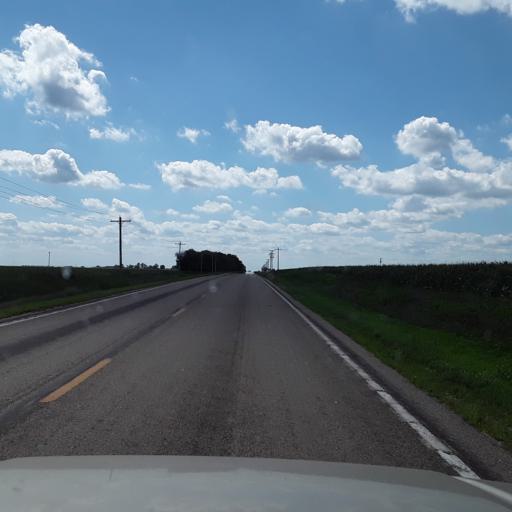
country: US
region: Nebraska
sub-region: Merrick County
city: Central City
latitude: 41.1910
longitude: -98.0172
